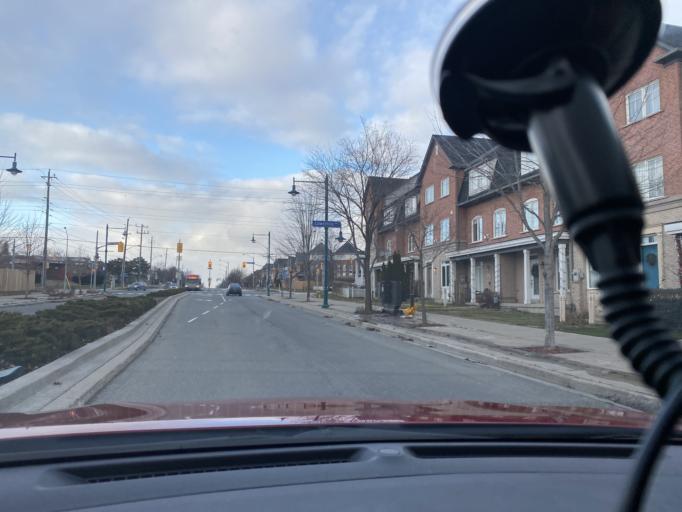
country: CA
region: Ontario
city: Scarborough
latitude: 43.7788
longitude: -79.1363
